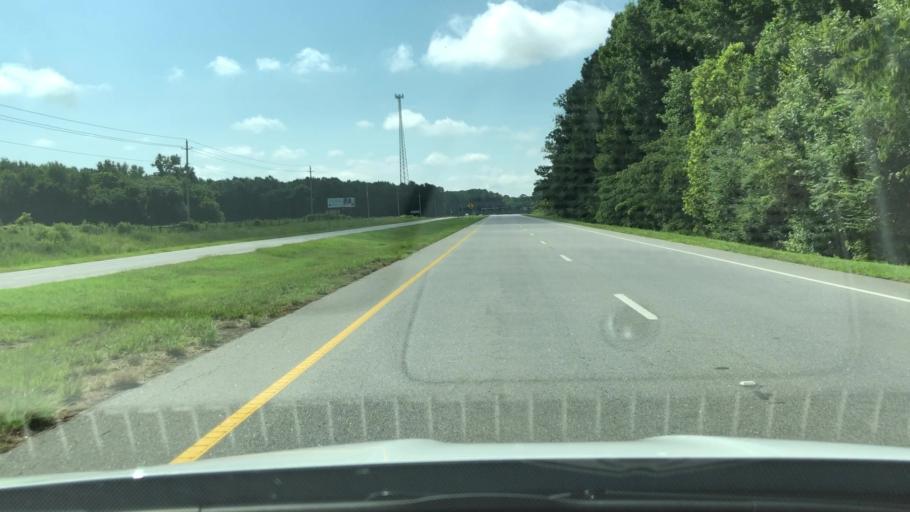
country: US
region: North Carolina
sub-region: Bertie County
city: Windsor
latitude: 35.9897
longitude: -76.9619
